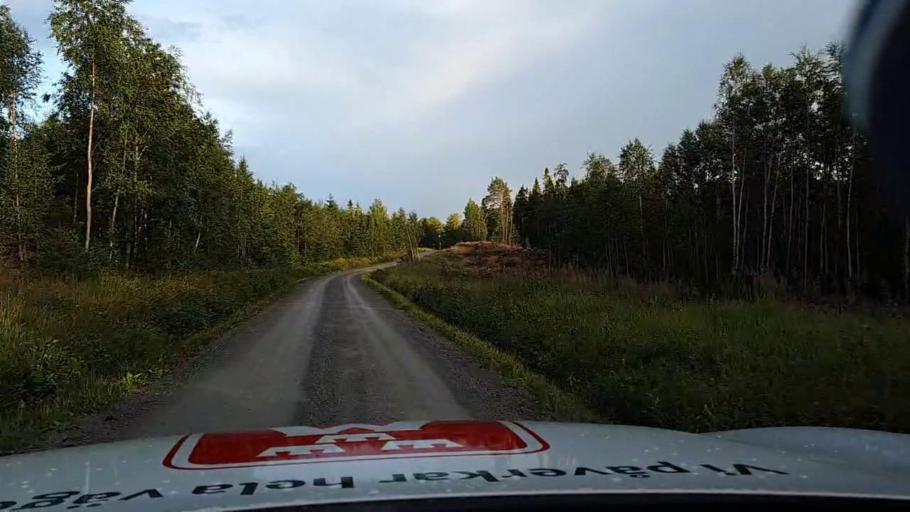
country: SE
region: Jaemtland
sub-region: Bergs Kommun
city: Hoverberg
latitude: 62.8569
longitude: 14.5352
